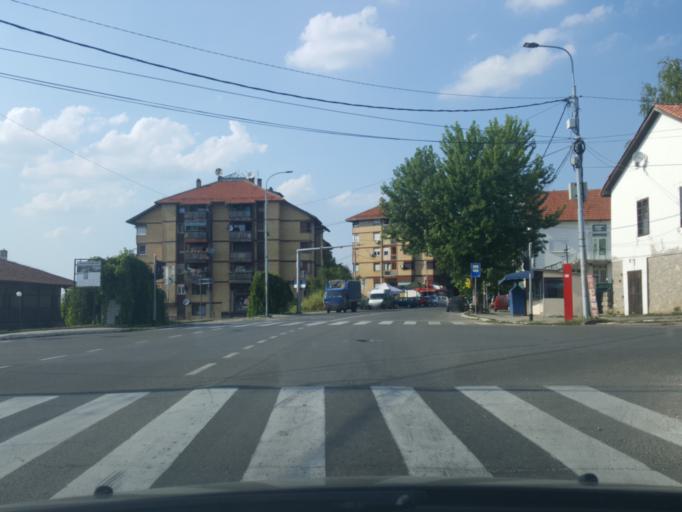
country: RS
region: Central Serbia
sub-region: Sumadijski Okrug
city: Topola
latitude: 44.2527
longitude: 20.6773
